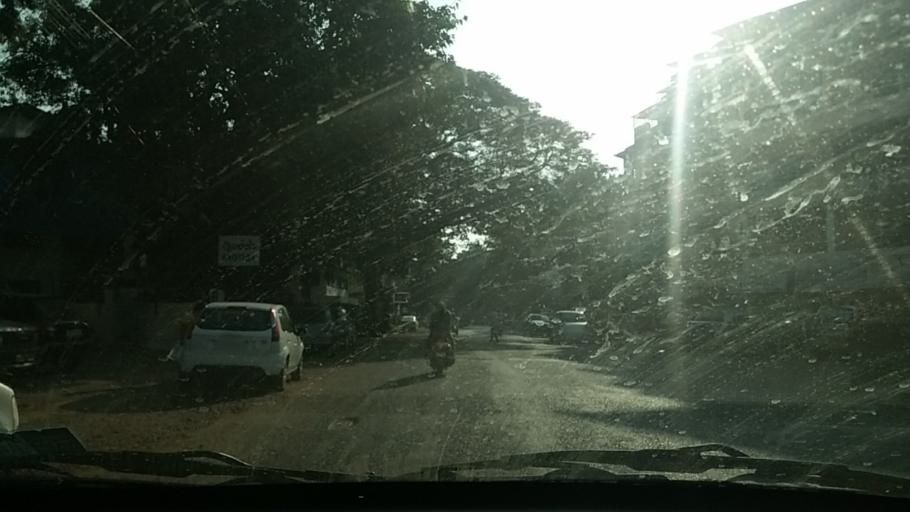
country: IN
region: Goa
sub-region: North Goa
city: Panaji
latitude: 15.4879
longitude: 73.8185
